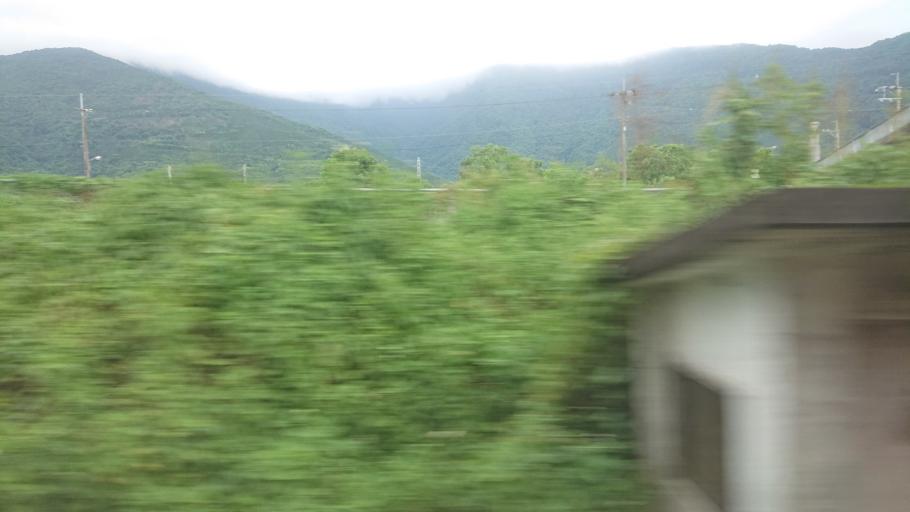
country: TW
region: Taiwan
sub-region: Hualien
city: Hualian
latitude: 23.7442
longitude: 121.4458
